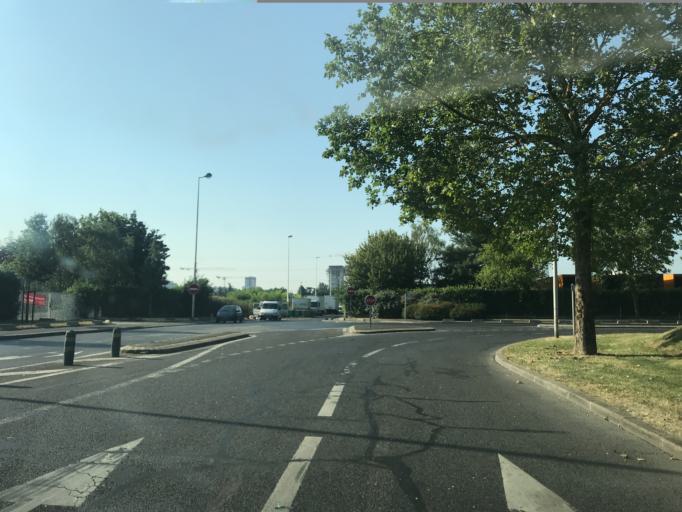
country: FR
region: Ile-de-France
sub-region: Departement des Hauts-de-Seine
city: Bois-Colombes
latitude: 48.9370
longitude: 2.2771
